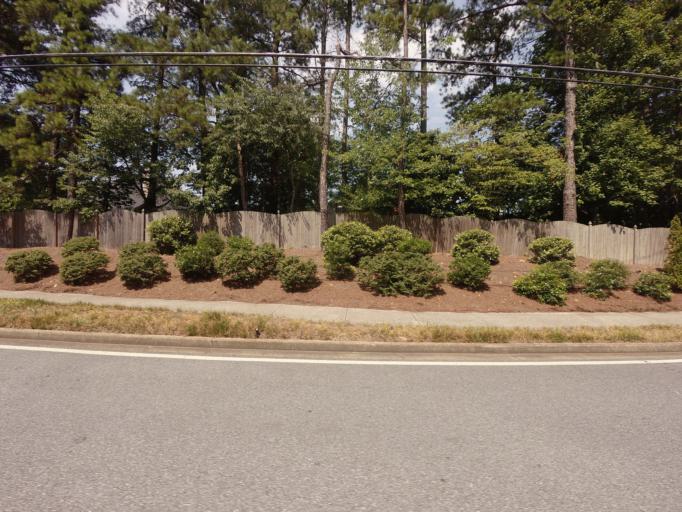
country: US
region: Georgia
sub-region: Fulton County
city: Johns Creek
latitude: 34.0148
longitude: -84.2637
